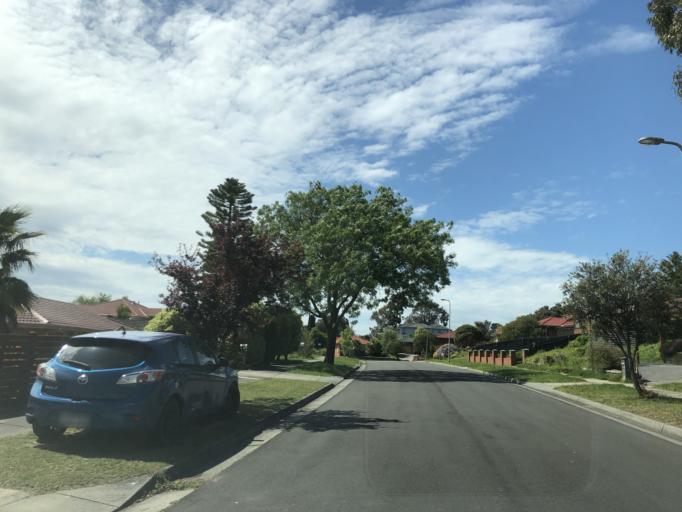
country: AU
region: Victoria
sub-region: Casey
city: Endeavour Hills
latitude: -37.9714
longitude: 145.2631
